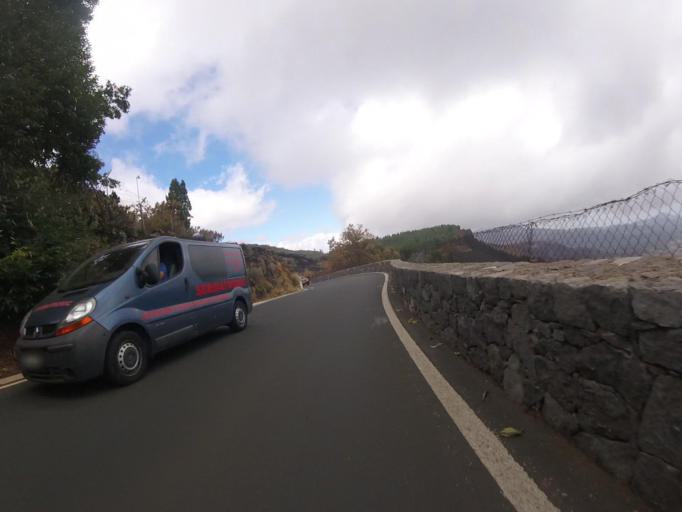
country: ES
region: Canary Islands
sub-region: Provincia de Las Palmas
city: San Bartolome
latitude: 27.9703
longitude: -15.5716
